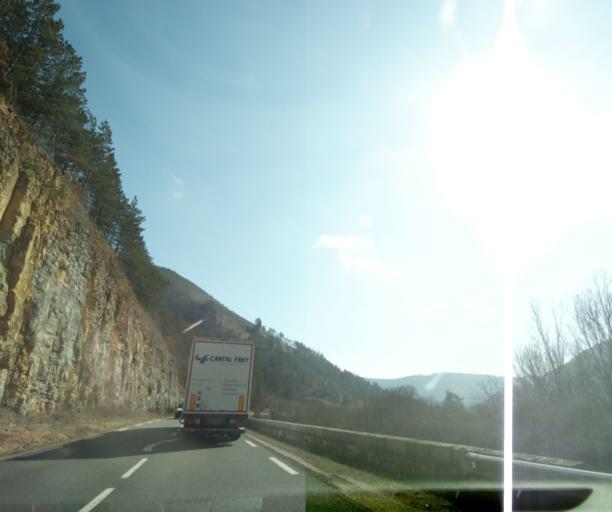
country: FR
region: Languedoc-Roussillon
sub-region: Departement de la Lozere
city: Chanac
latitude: 44.4929
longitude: 3.4161
